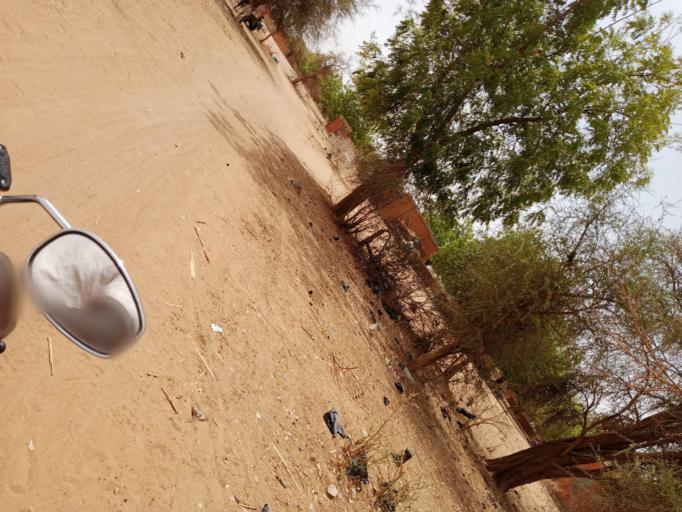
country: BF
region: Est
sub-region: Gnagna Province
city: Bogande
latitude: 13.0831
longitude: -0.0061
